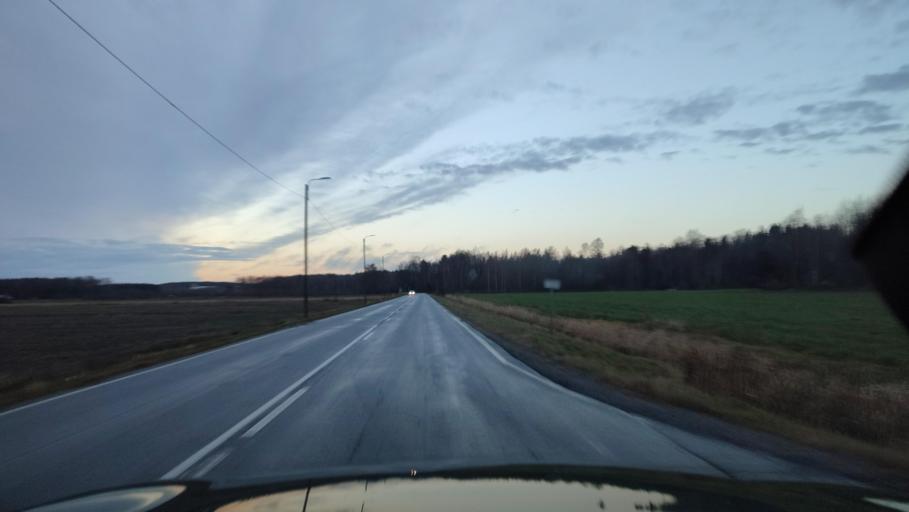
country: FI
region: Ostrobothnia
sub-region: Vaasa
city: Ristinummi
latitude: 63.0460
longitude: 21.7457
